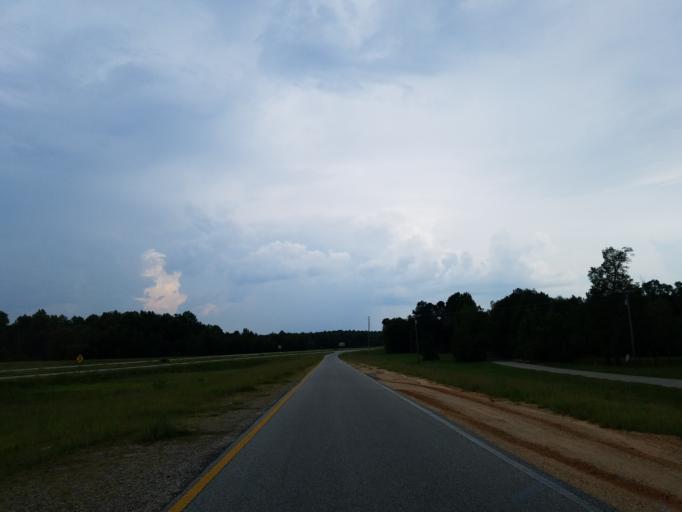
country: US
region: Mississippi
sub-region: Wayne County
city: Belmont
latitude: 31.4361
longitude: -88.4668
